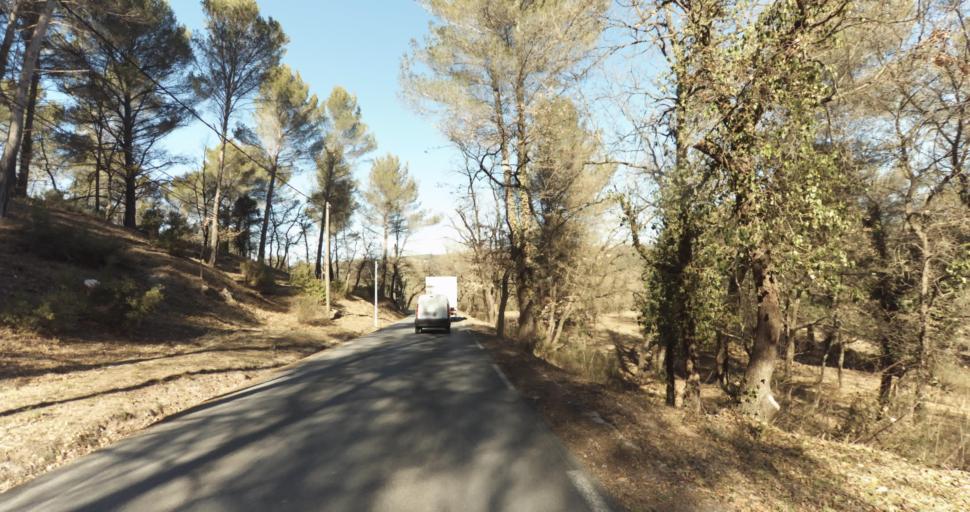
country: FR
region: Provence-Alpes-Cote d'Azur
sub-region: Departement des Bouches-du-Rhone
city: Peypin
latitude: 43.3920
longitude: 5.5716
